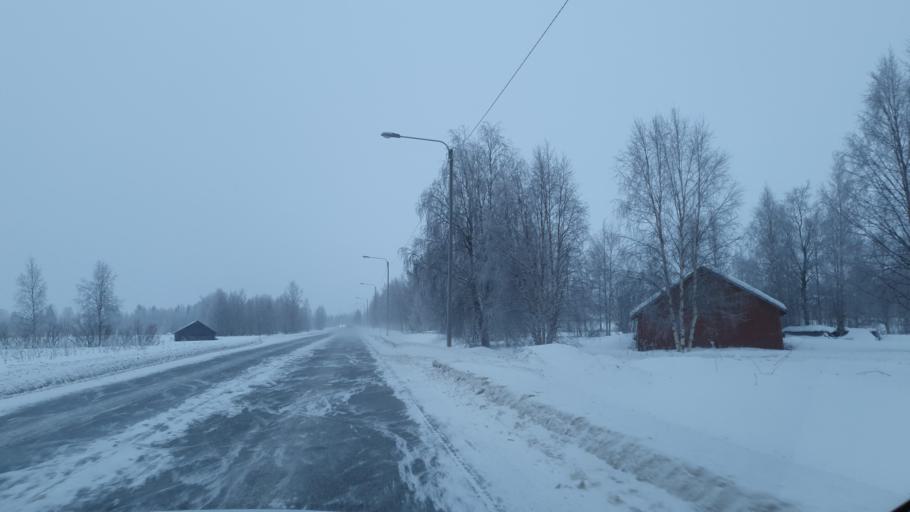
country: FI
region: Lapland
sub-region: Kemi-Tornio
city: Tornio
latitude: 66.0724
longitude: 23.9837
